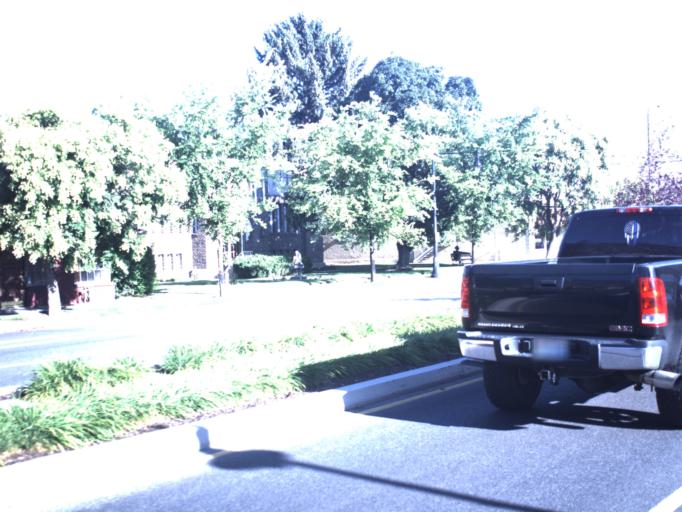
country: US
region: Utah
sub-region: Utah County
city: Springville
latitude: 40.1647
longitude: -111.6107
